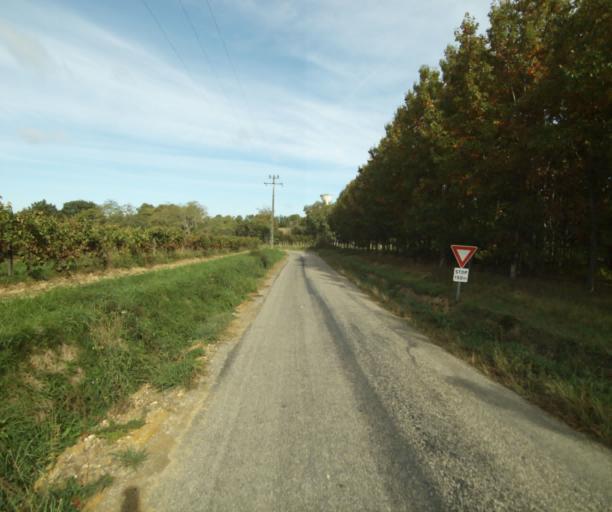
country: FR
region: Midi-Pyrenees
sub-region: Departement du Gers
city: Eauze
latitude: 43.8706
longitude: 0.1257
